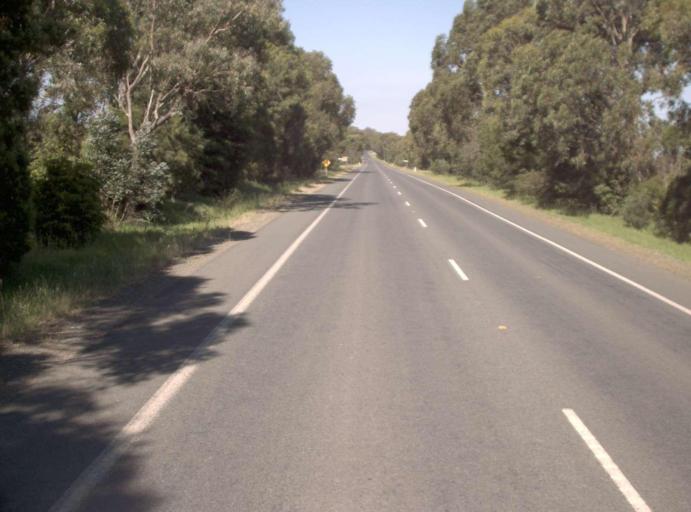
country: AU
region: Victoria
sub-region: Latrobe
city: Traralgon
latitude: -38.5488
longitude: 146.6896
